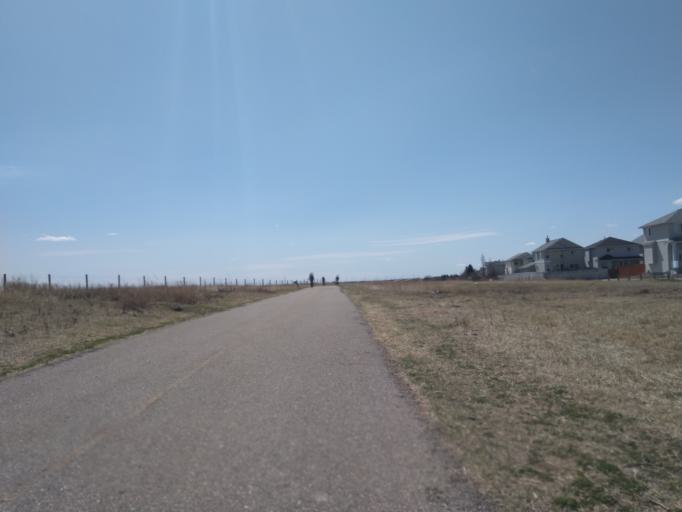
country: CA
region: Alberta
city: Chestermere
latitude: 51.0905
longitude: -113.9240
